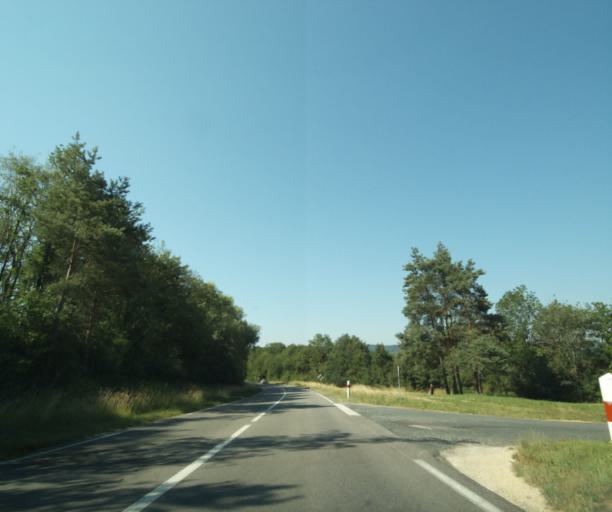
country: FR
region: Lorraine
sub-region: Departement de Meurthe-et-Moselle
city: Ecrouves
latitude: 48.6459
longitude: 5.8674
